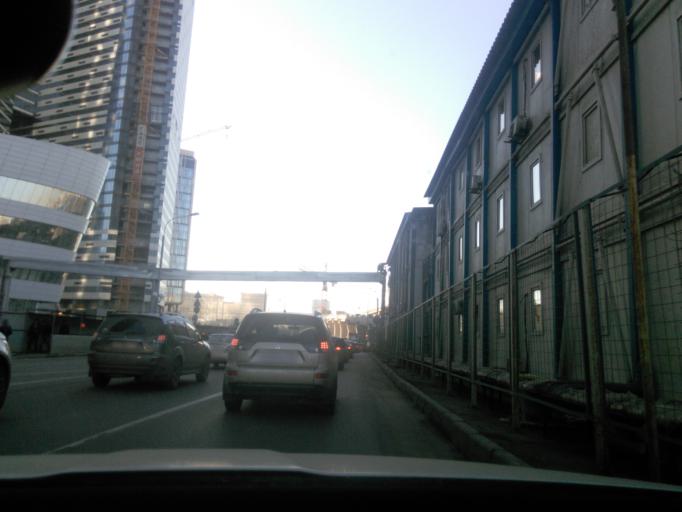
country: RU
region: Moskovskaya
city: Presnenskiy
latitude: 55.7495
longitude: 37.5333
